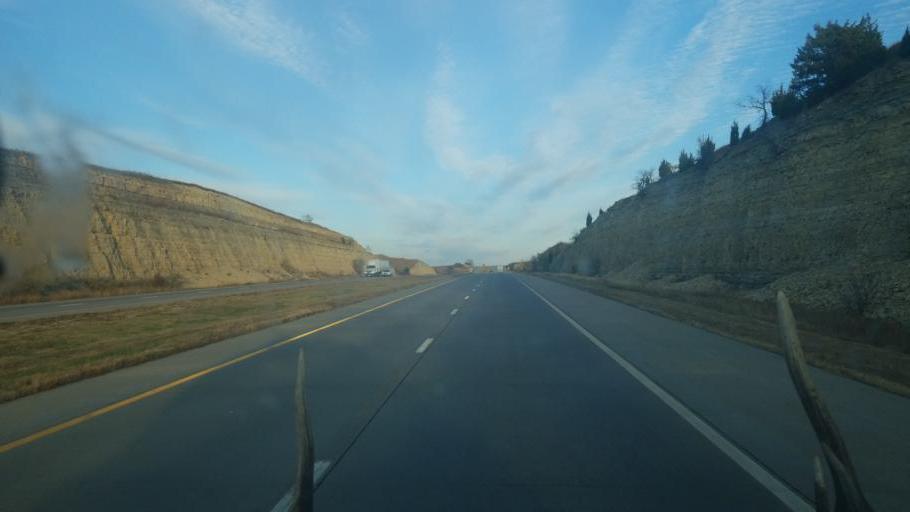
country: US
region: Kansas
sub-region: Riley County
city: Ogden
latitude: 39.0635
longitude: -96.7046
